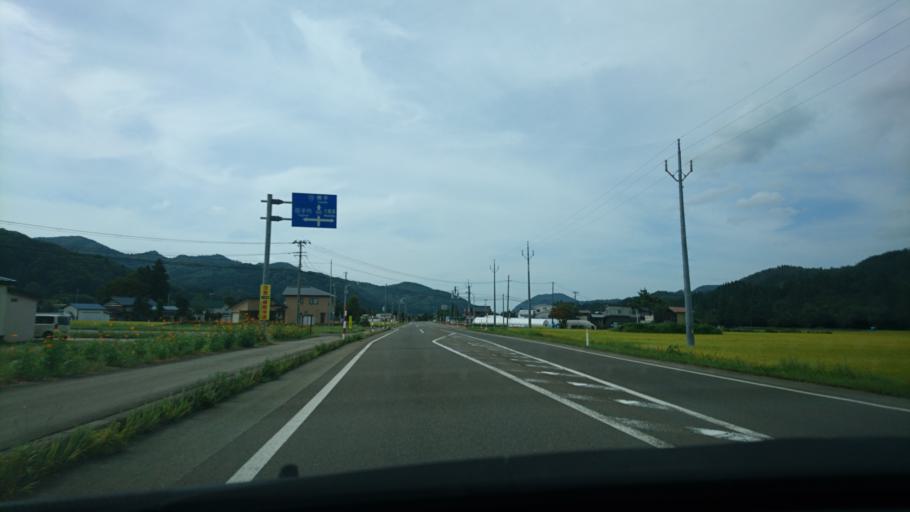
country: JP
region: Akita
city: Yuzawa
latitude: 39.1836
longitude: 140.6410
